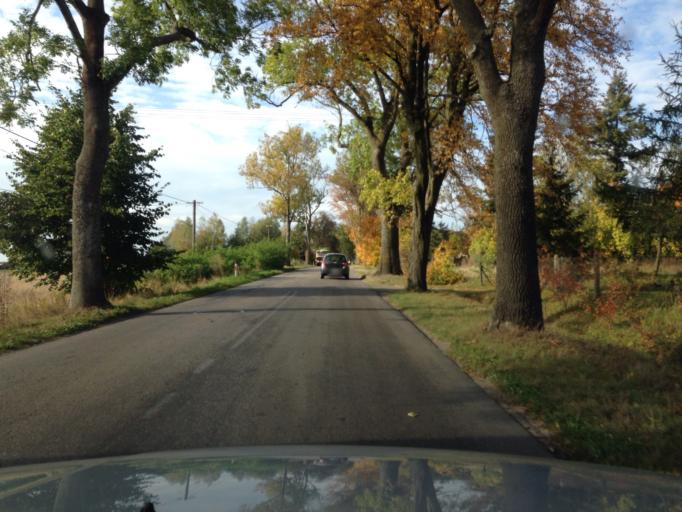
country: PL
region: Pomeranian Voivodeship
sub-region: Powiat koscierski
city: Stara Kiszewa
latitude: 53.9929
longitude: 18.1540
